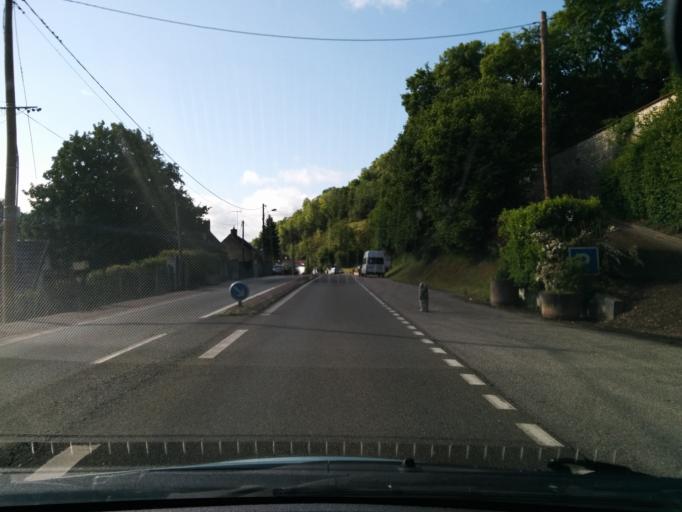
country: FR
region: Ile-de-France
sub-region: Departement des Yvelines
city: Limetz-Villez
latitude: 49.0632
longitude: 1.5221
